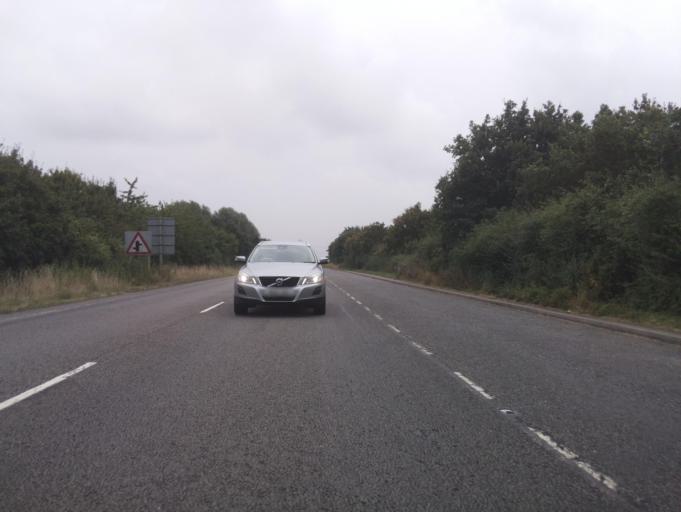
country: GB
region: England
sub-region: Nottinghamshire
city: South Collingham
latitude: 53.0897
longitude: -0.7607
